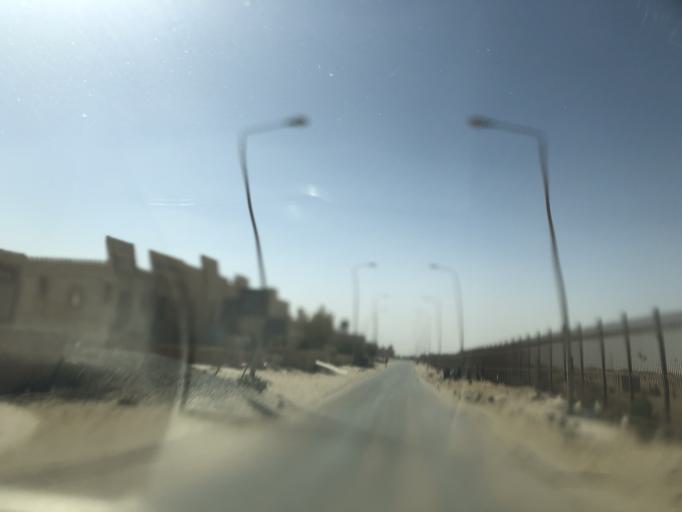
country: EG
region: Al Jizah
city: Madinat Sittah Uktubar
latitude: 29.9266
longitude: 30.9520
